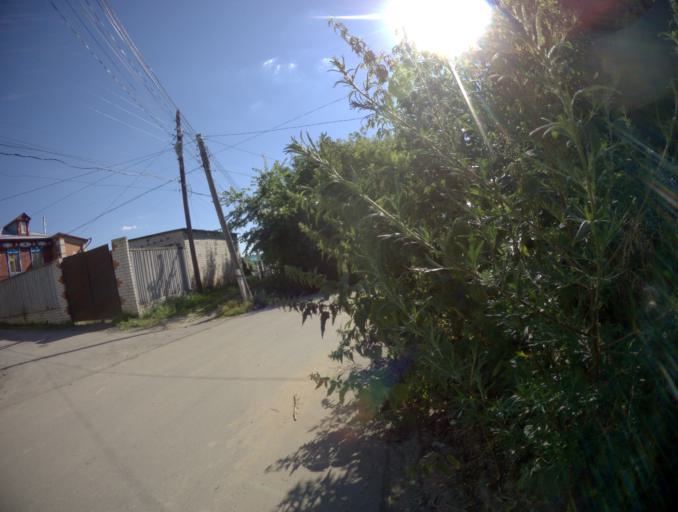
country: RU
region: Nizjnij Novgorod
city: Pavlovo
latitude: 55.9733
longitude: 43.0797
